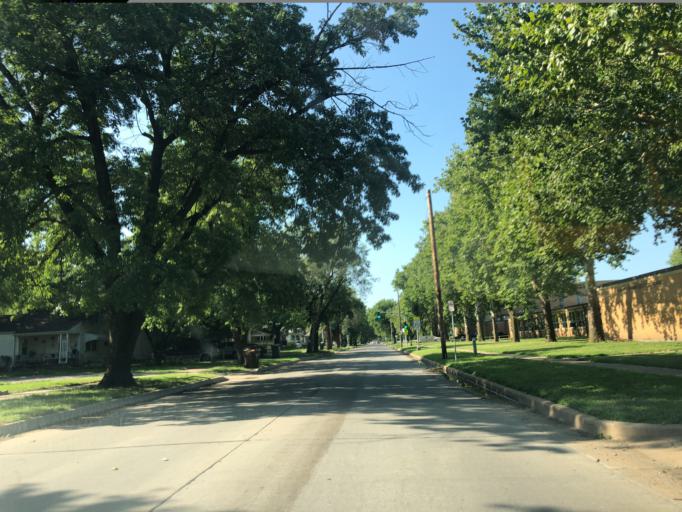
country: US
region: Kansas
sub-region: Sedgwick County
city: Wichita
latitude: 37.7208
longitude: -97.3447
